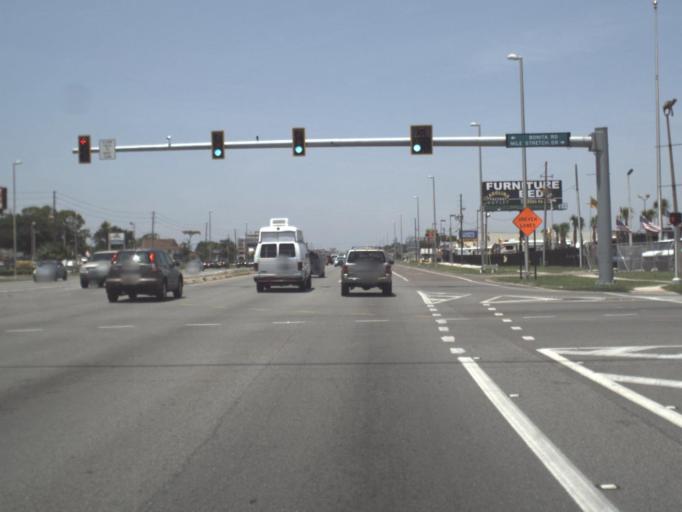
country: US
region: Florida
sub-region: Pasco County
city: Holiday
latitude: 28.1877
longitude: -82.7399
